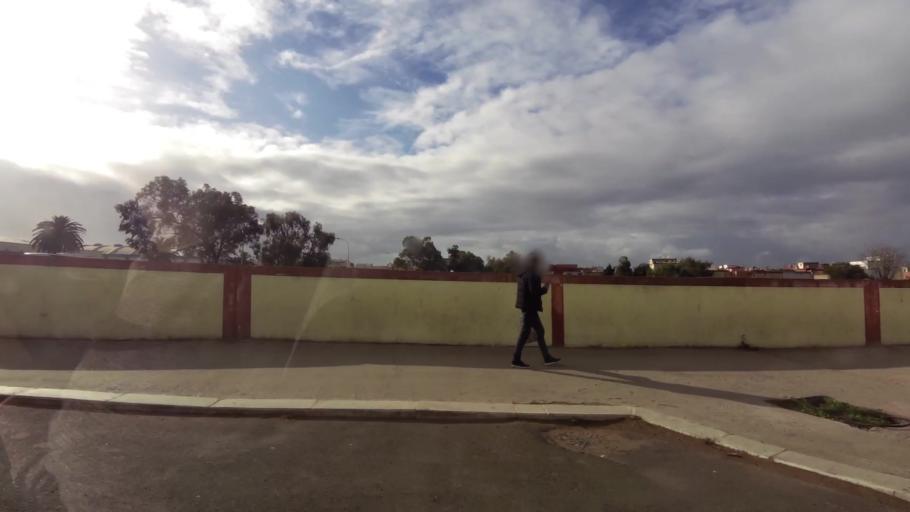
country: MA
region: Doukkala-Abda
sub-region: El-Jadida
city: El Jadida
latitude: 33.2454
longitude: -8.5201
